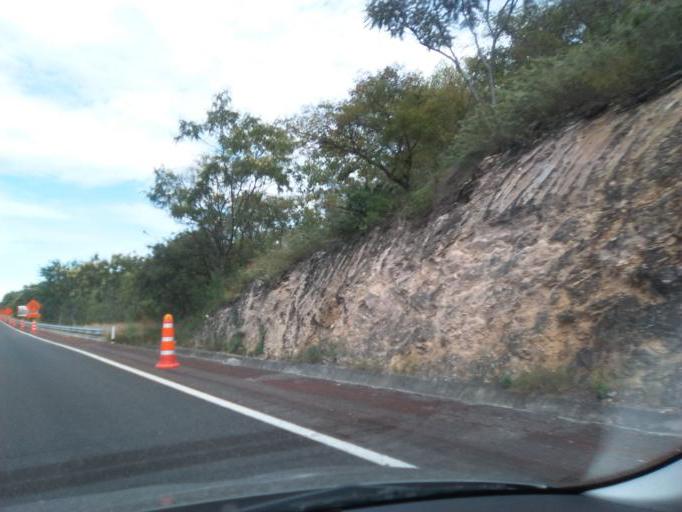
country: MX
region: Guerrero
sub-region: Eduardo Neri
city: Axaxacualco
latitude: 17.8019
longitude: -99.4732
